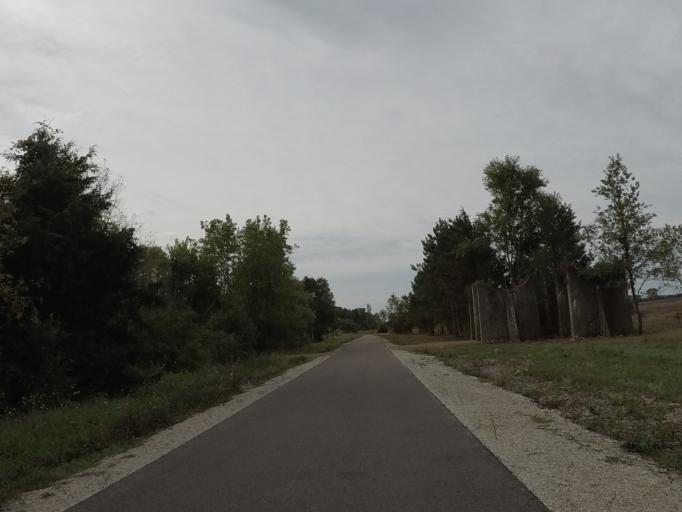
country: US
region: Wisconsin
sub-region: Sauk County
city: Prairie du Sac
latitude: 43.3720
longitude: -89.7357
